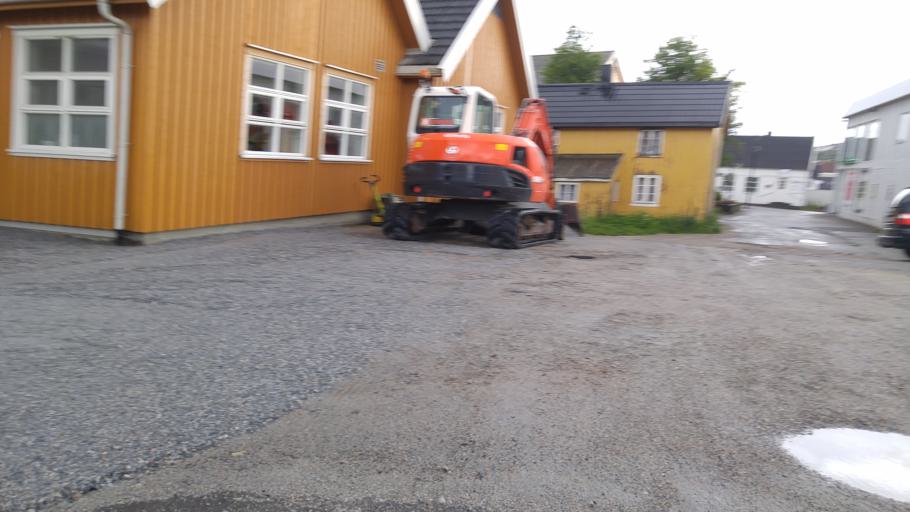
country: NO
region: Nord-Trondelag
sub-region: Vikna
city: Rorvik
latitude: 64.8624
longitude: 11.2382
